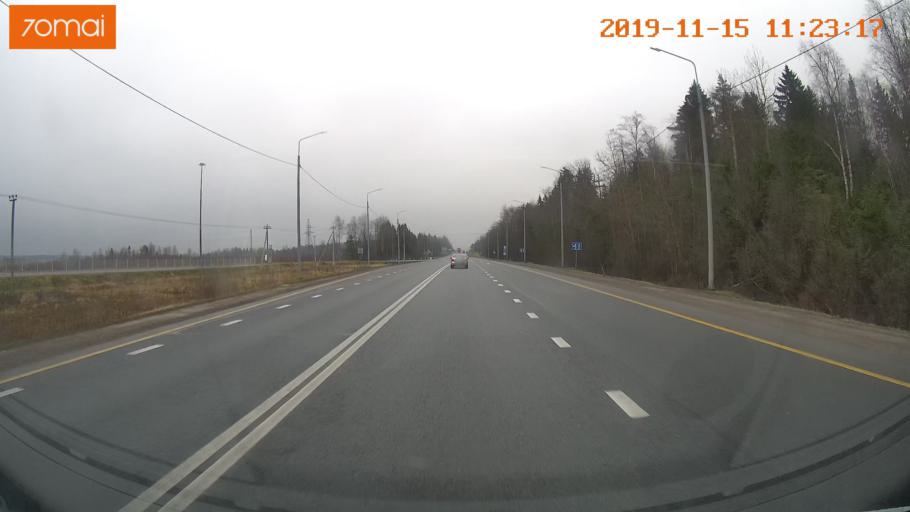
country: RU
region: Vologda
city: Molochnoye
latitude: 59.1506
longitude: 39.3786
